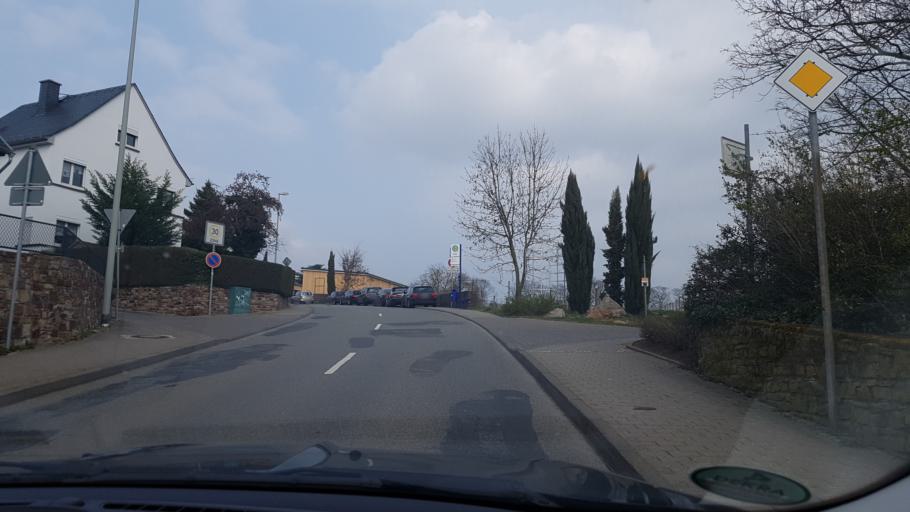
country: DE
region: Hesse
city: Geisenheim
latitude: 50.0016
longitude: 7.9806
